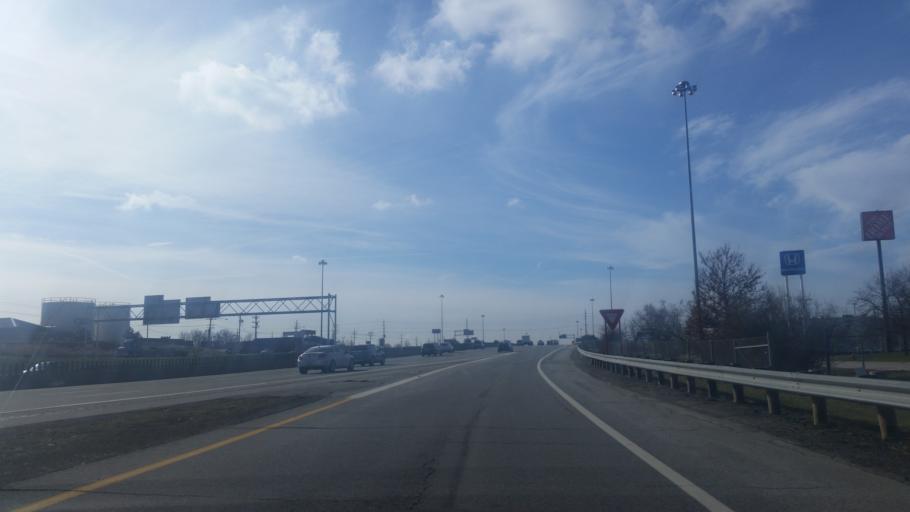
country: US
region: Ohio
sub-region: Cuyahoga County
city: Euclid
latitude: 41.5835
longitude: -81.5361
